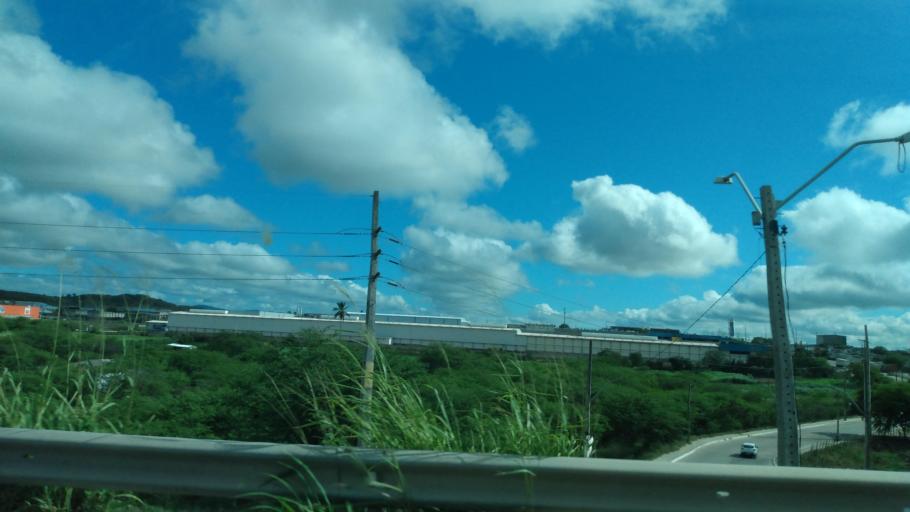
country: BR
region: Pernambuco
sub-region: Caruaru
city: Caruaru
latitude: -8.3049
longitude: -36.0112
